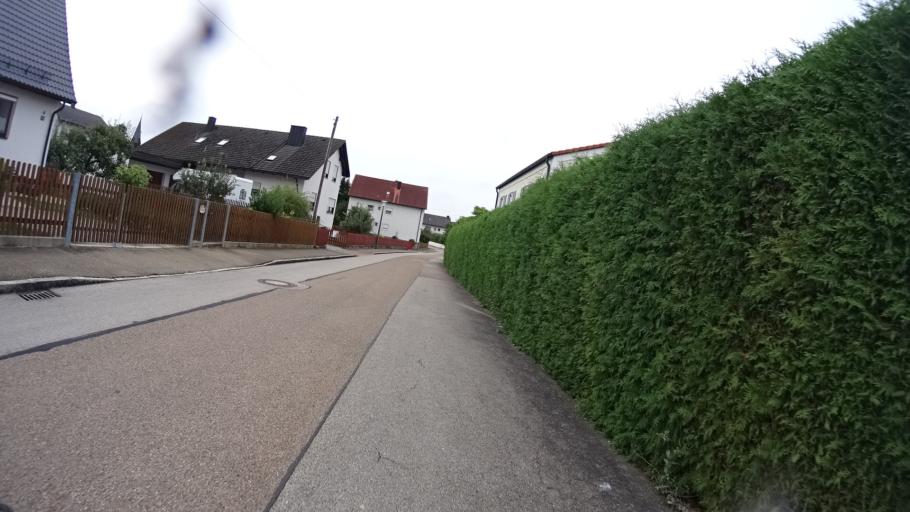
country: DE
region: Bavaria
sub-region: Upper Bavaria
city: Gaimersheim
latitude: 48.8360
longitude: 11.3562
